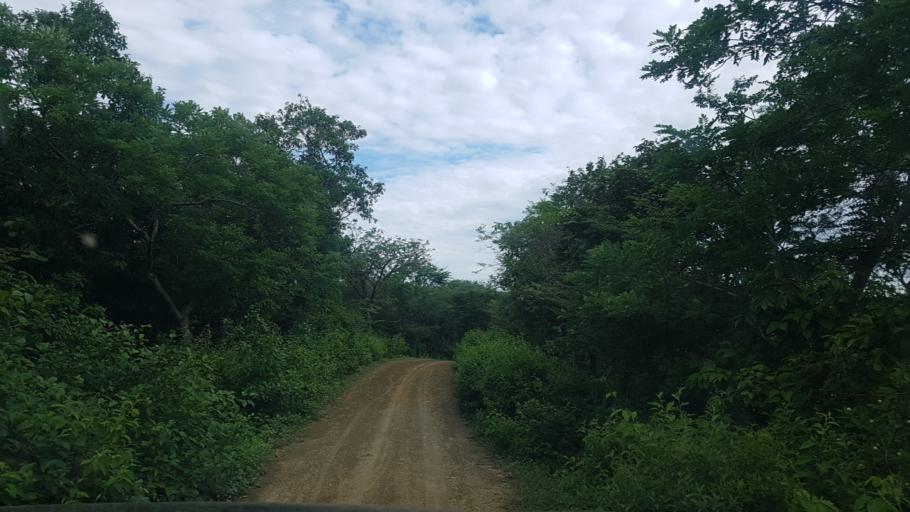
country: NI
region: Nueva Segovia
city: Ciudad Antigua
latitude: 13.5937
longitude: -86.3703
